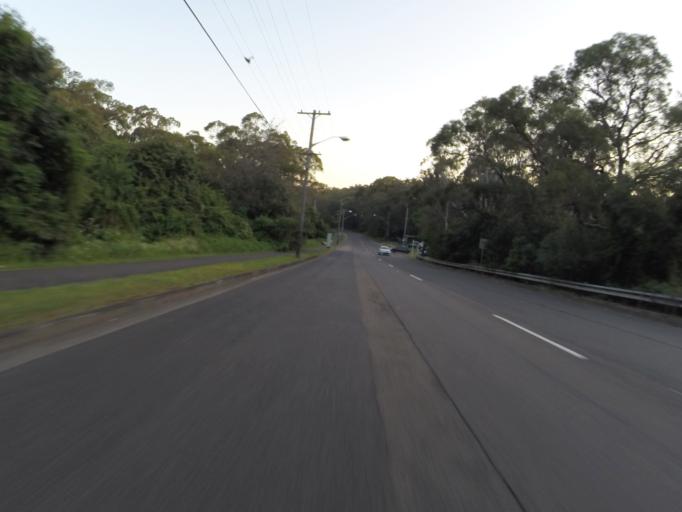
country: AU
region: New South Wales
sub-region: Bankstown
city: Revesby
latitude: -33.9680
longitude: 151.0152
